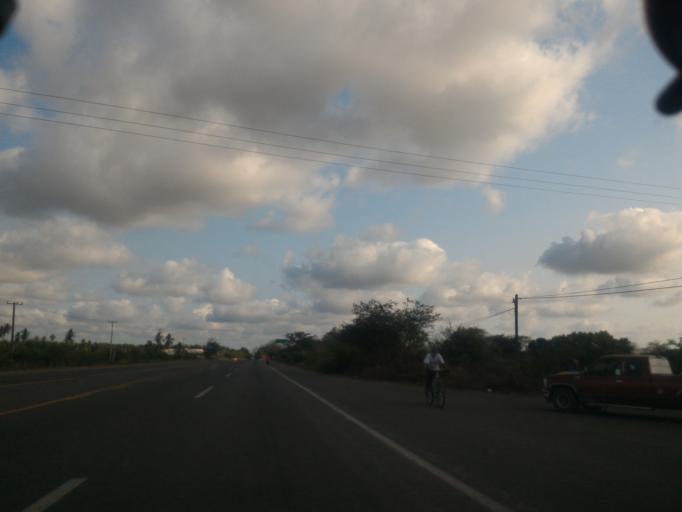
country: MX
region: Colima
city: Tecoman
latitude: 18.8928
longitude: -103.8563
